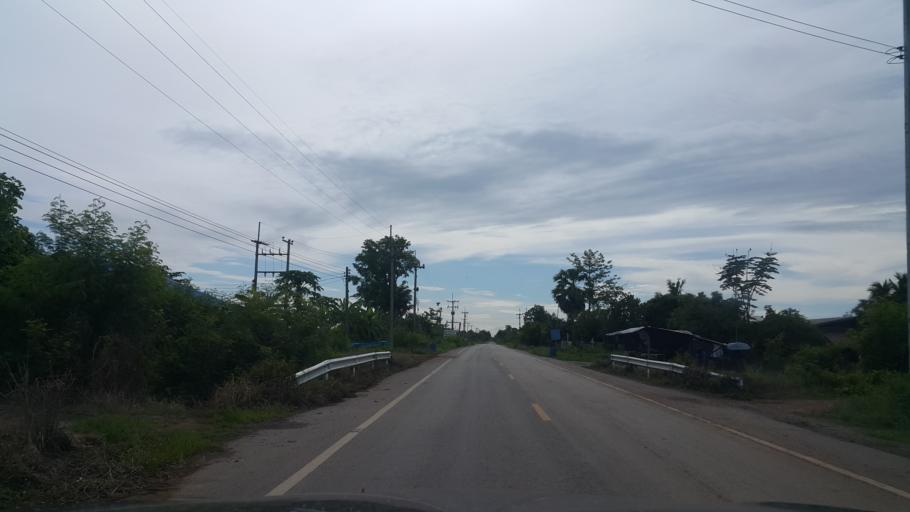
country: TH
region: Sukhothai
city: Si Nakhon
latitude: 17.2625
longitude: 99.9326
